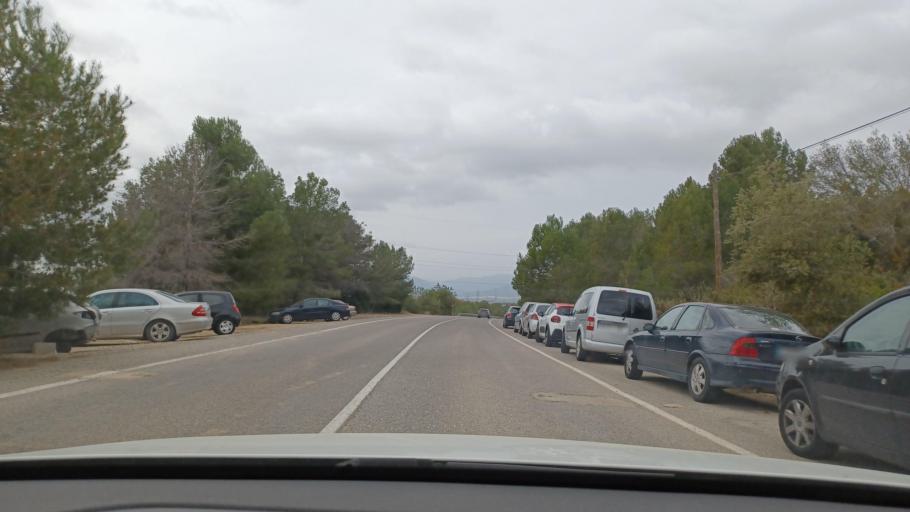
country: ES
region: Catalonia
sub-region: Provincia de Tarragona
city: La Secuita
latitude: 41.1931
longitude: 1.2687
